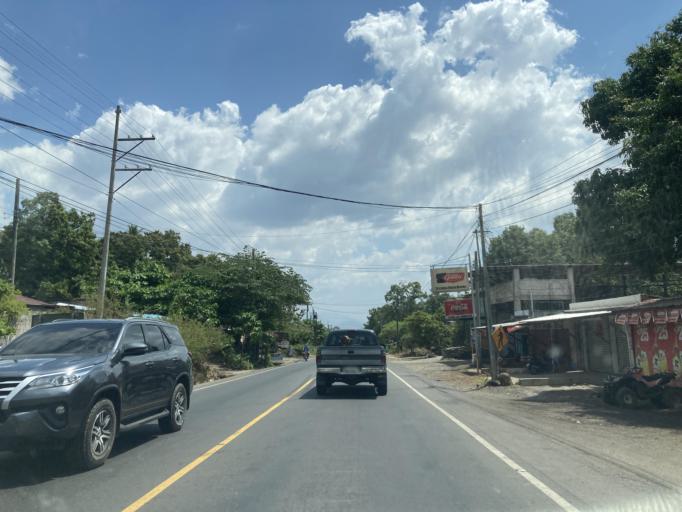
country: GT
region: Santa Rosa
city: Guazacapan
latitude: 14.0678
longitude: -90.4127
